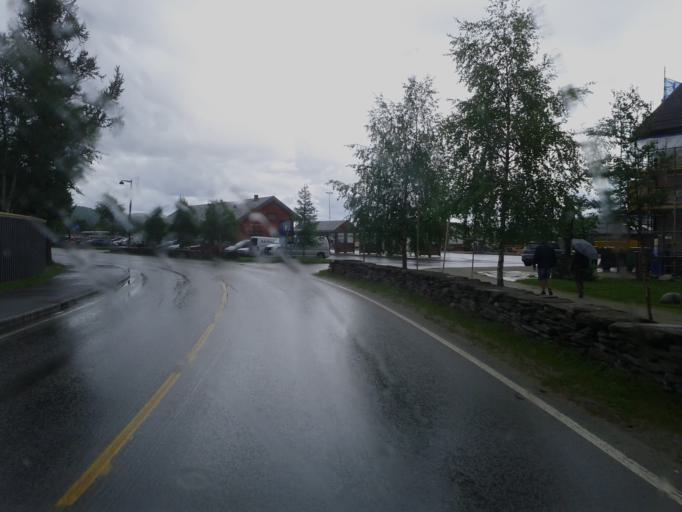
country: NO
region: Sor-Trondelag
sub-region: Roros
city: Roros
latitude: 62.5752
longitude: 11.3790
